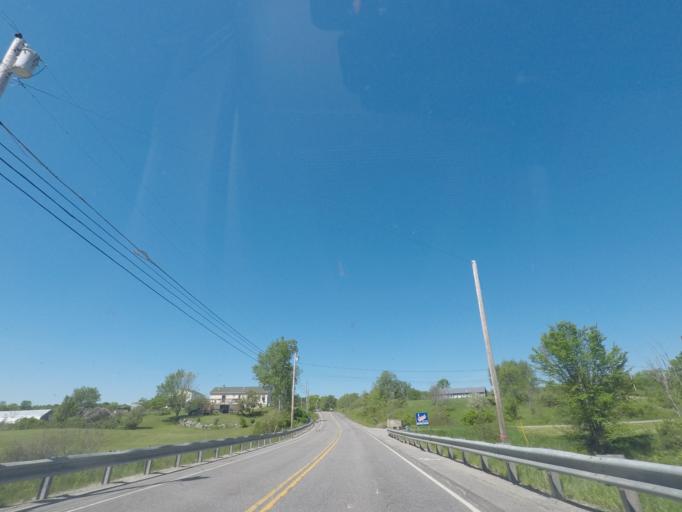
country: US
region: Maine
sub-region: Kennebec County
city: Gardiner
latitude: 44.2274
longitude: -69.8398
